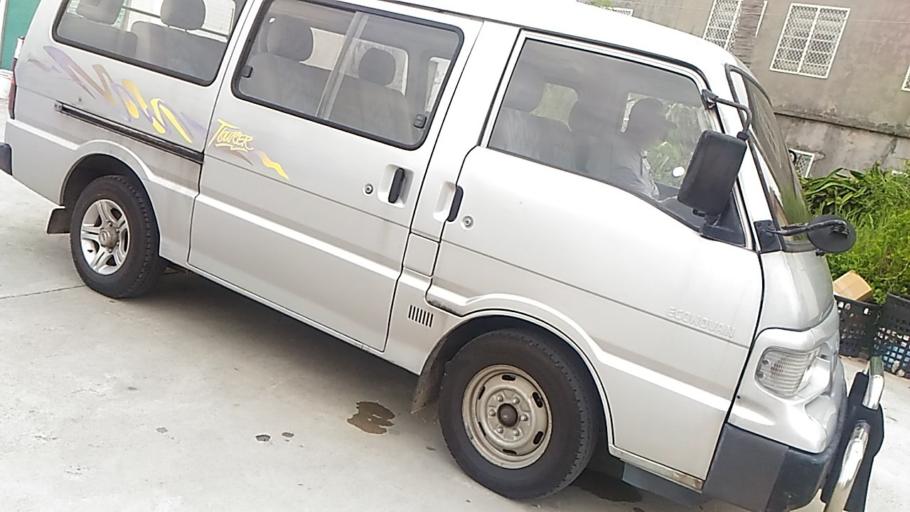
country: TW
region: Taiwan
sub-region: Penghu
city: Ma-kung
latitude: 23.3721
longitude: 119.4958
